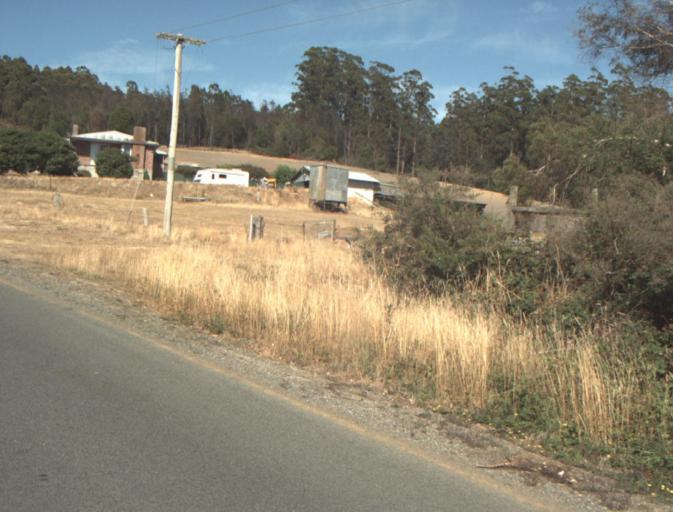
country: AU
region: Tasmania
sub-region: Launceston
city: Mayfield
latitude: -41.1993
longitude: 147.2176
